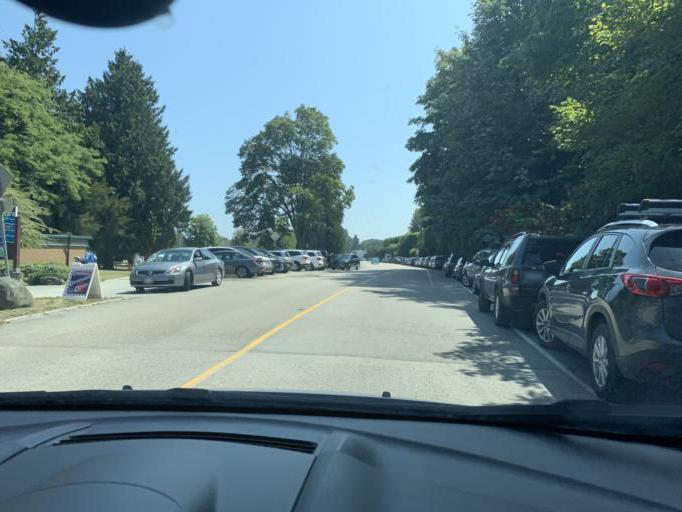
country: CA
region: British Columbia
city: West End
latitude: 49.2761
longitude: -123.2153
